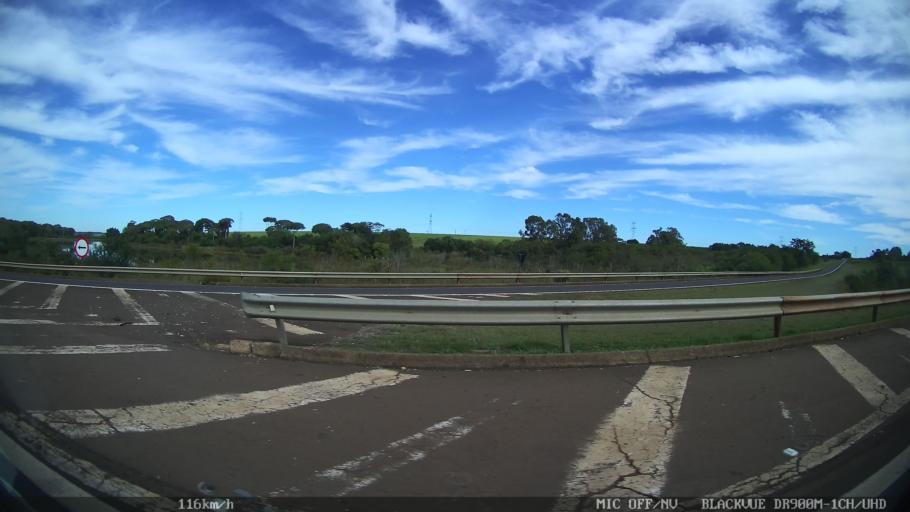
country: BR
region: Sao Paulo
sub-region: Taquaritinga
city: Taquaritinga
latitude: -21.4786
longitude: -48.5944
